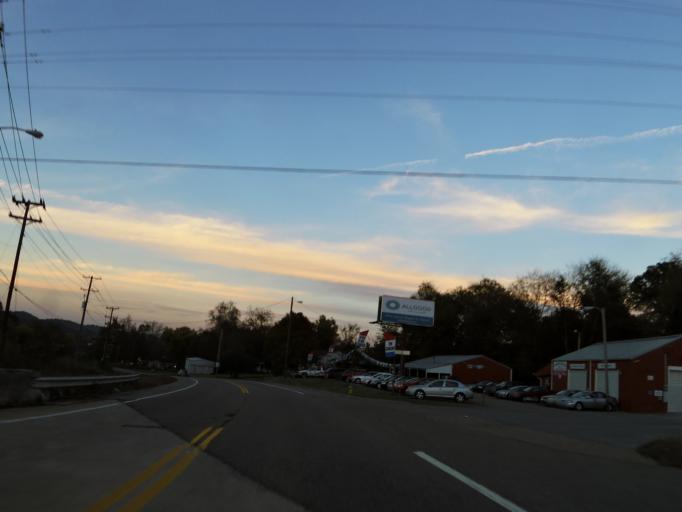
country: US
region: Tennessee
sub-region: Knox County
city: Knoxville
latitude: 35.9207
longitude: -83.9264
